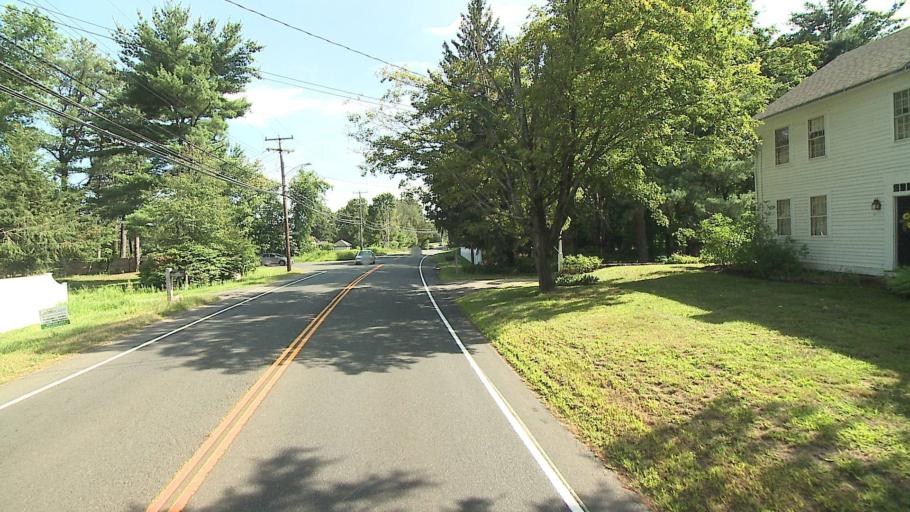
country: US
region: Connecticut
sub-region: Hartford County
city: Farmington
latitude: 41.7719
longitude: -72.8606
